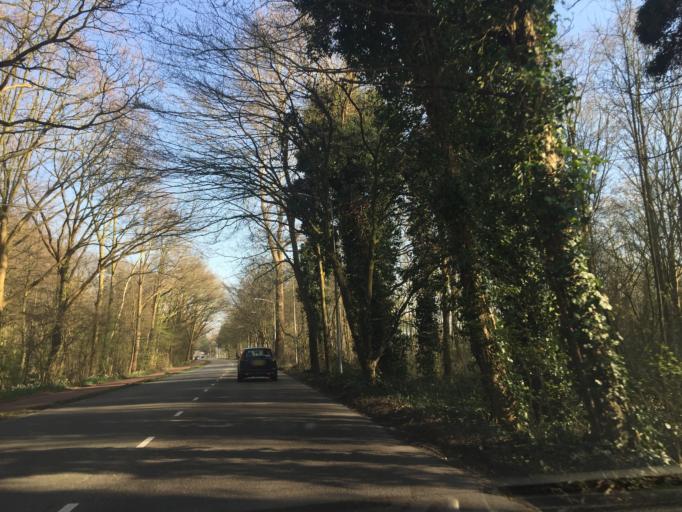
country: NL
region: South Holland
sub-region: Gemeente Oegstgeest
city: Oegstgeest
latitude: 52.1796
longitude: 4.4812
